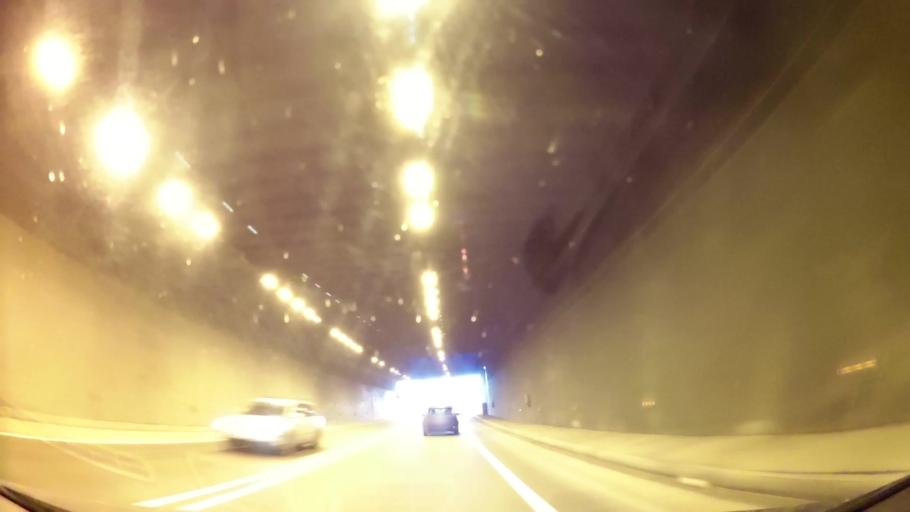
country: RS
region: Central Serbia
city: Sremcica
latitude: 44.7112
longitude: 20.3681
